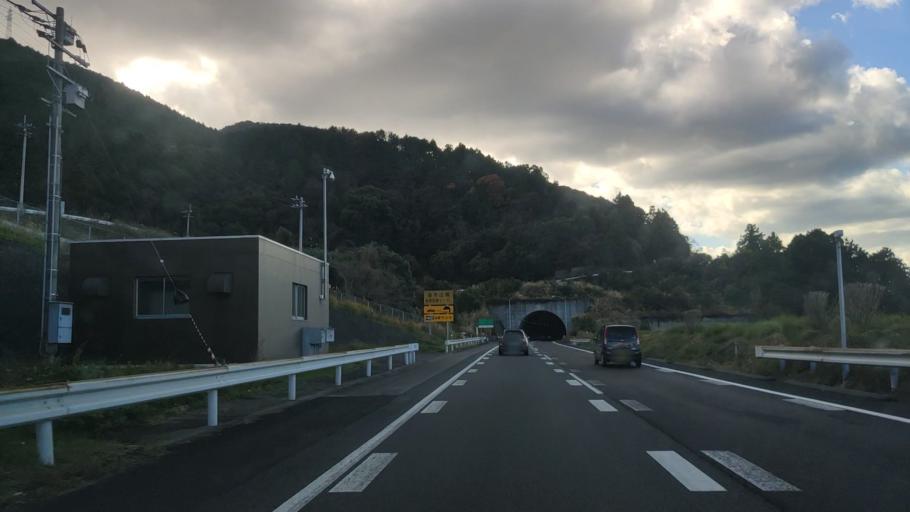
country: JP
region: Ehime
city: Kawanoecho
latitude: 33.9664
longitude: 133.5418
